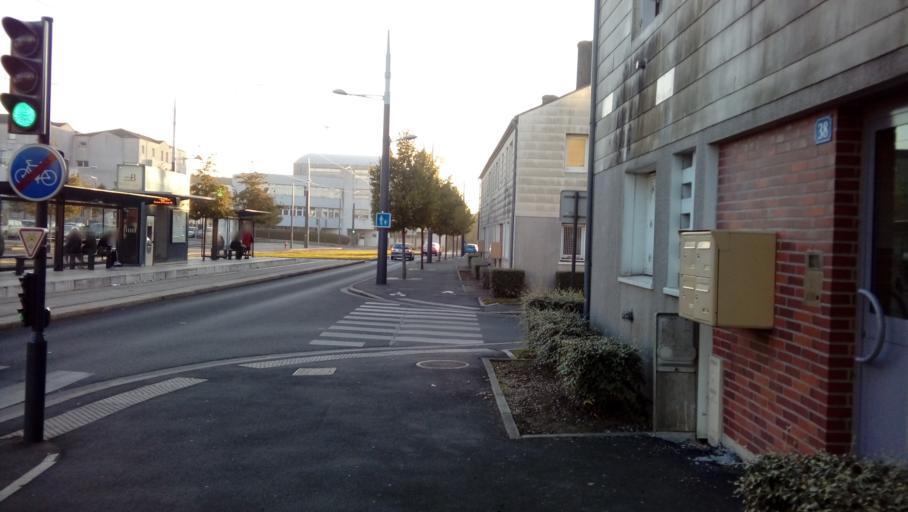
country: FR
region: Centre
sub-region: Departement du Loiret
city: Saint-Jean-le-Blanc
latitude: 47.9114
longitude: 1.9281
